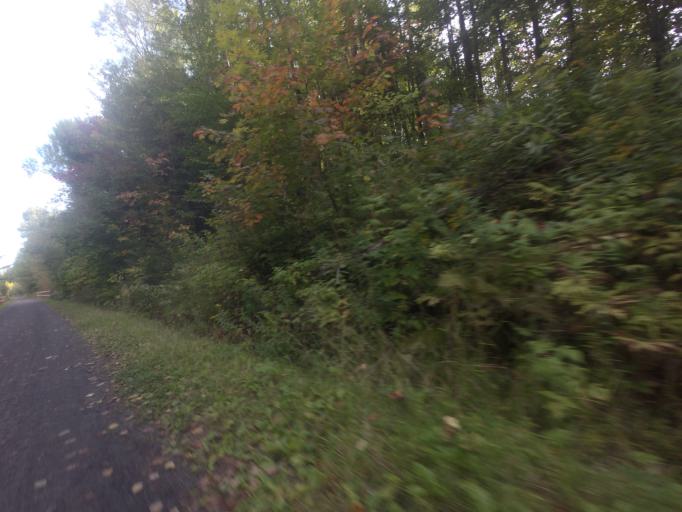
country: CA
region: Quebec
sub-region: Laurentides
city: Sainte-Adele
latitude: 45.9327
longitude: -74.1217
